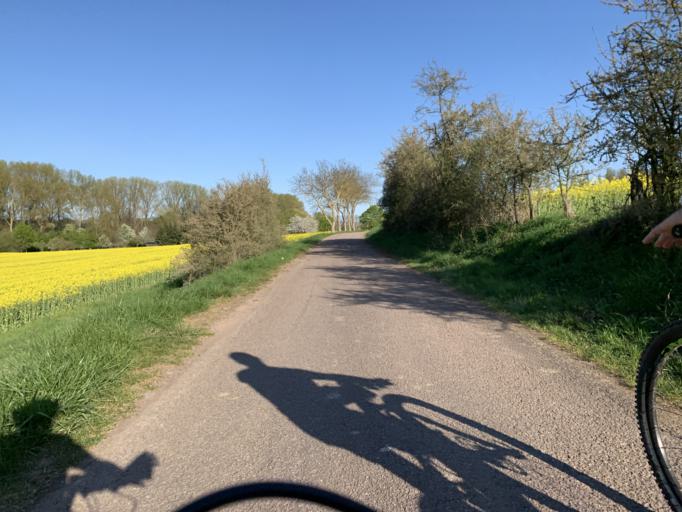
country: DE
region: Rheinland-Pfalz
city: Langenlonsheim
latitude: 49.8880
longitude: 7.8834
